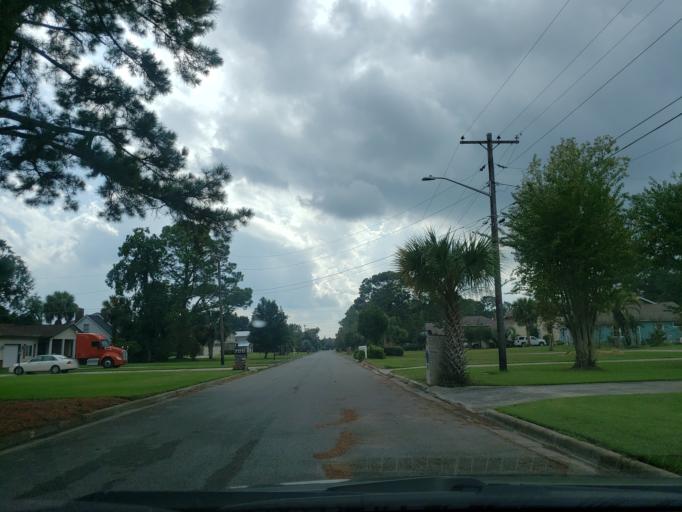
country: US
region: Georgia
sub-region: Chatham County
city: Skidaway Island
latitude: 31.9297
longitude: -81.0840
